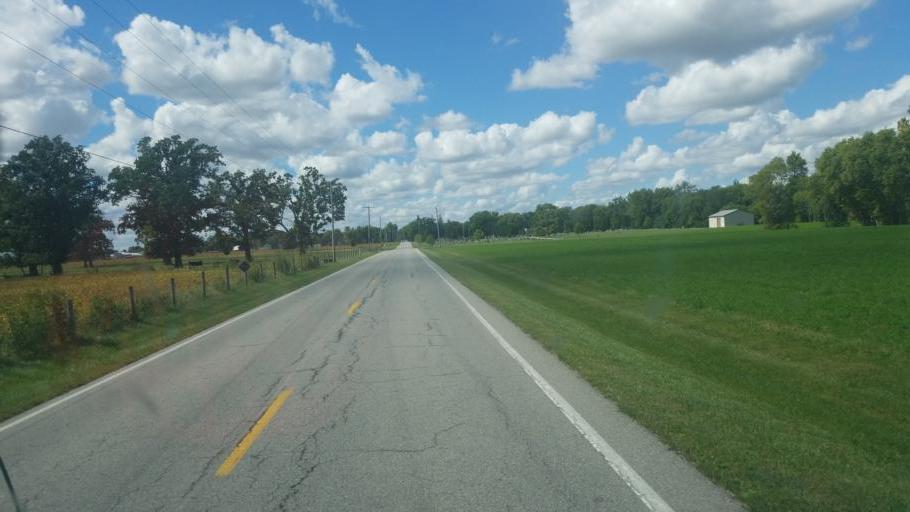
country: US
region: Ohio
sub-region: Union County
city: Marysville
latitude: 40.1749
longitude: -83.4219
